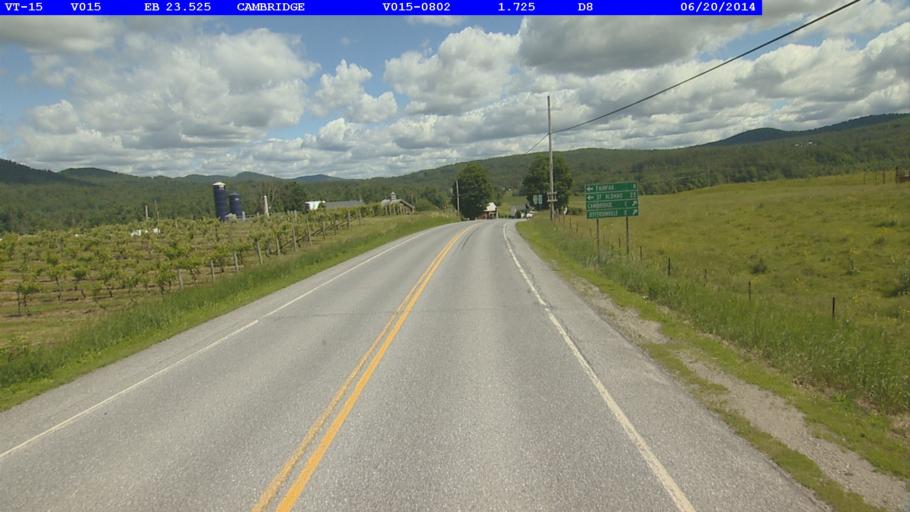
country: US
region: Vermont
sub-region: Chittenden County
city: Jericho
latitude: 44.6460
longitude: -72.8898
